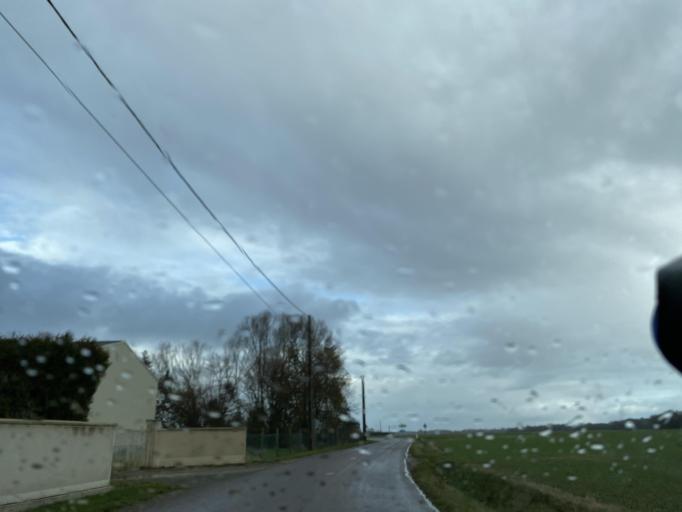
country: FR
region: Haute-Normandie
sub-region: Departement de l'Eure
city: Tillieres-sur-Avre
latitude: 48.7872
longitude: 1.0612
